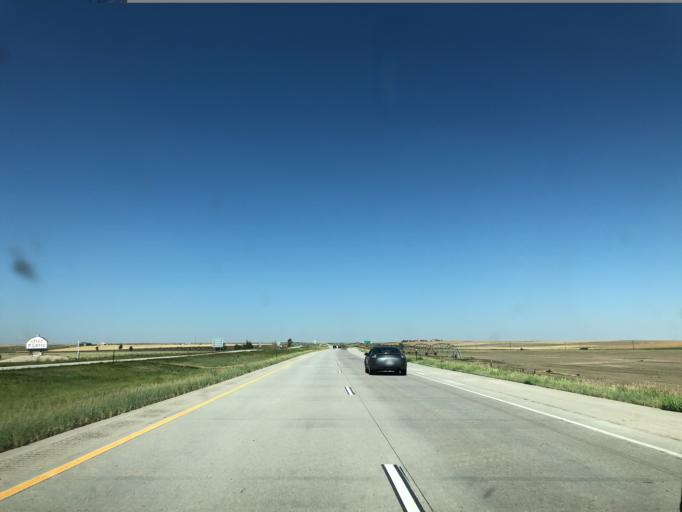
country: US
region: Colorado
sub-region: Arapahoe County
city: Byers
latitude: 39.7198
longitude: -104.2379
